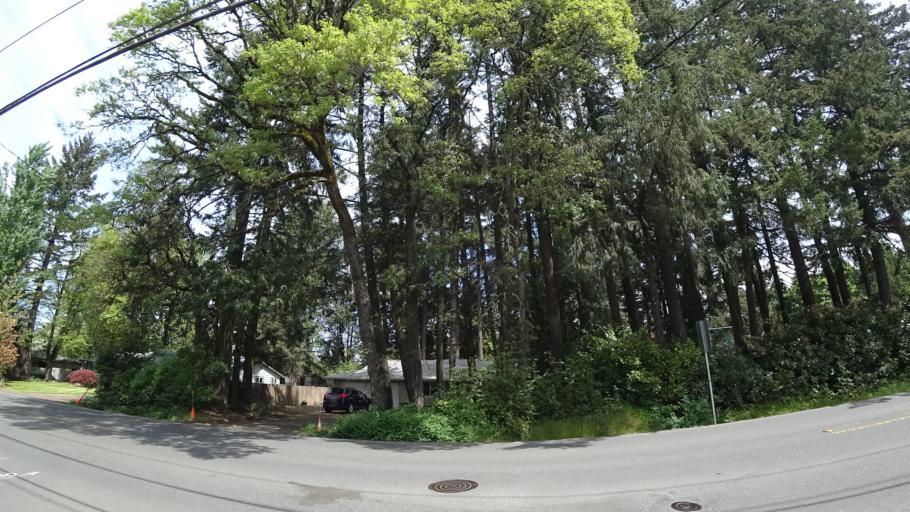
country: US
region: Oregon
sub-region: Washington County
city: Aloha
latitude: 45.4796
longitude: -122.8818
